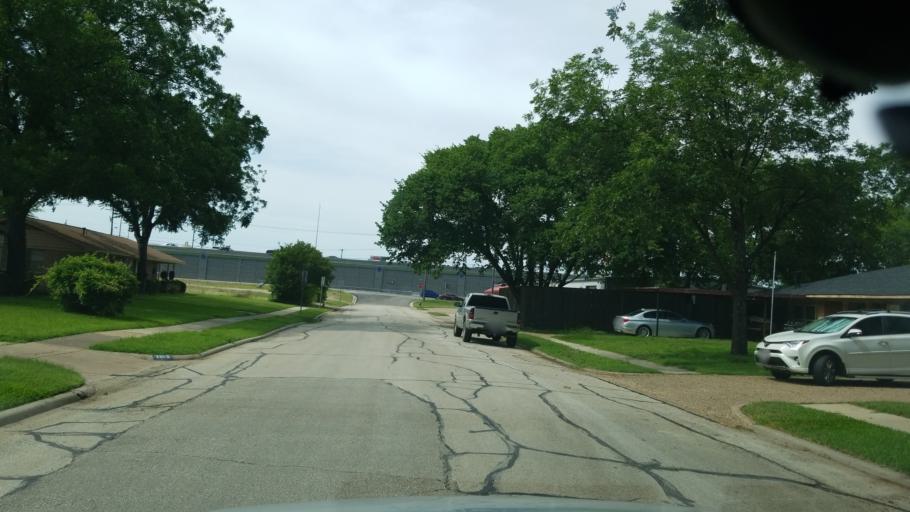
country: US
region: Texas
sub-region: Dallas County
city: Irving
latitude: 32.8355
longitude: -96.9522
